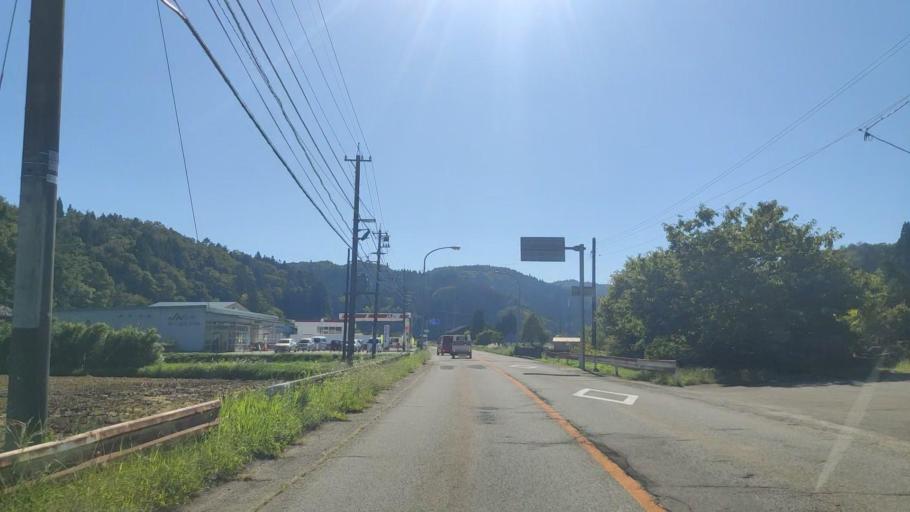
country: JP
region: Ishikawa
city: Nanao
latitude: 37.3369
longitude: 137.2108
